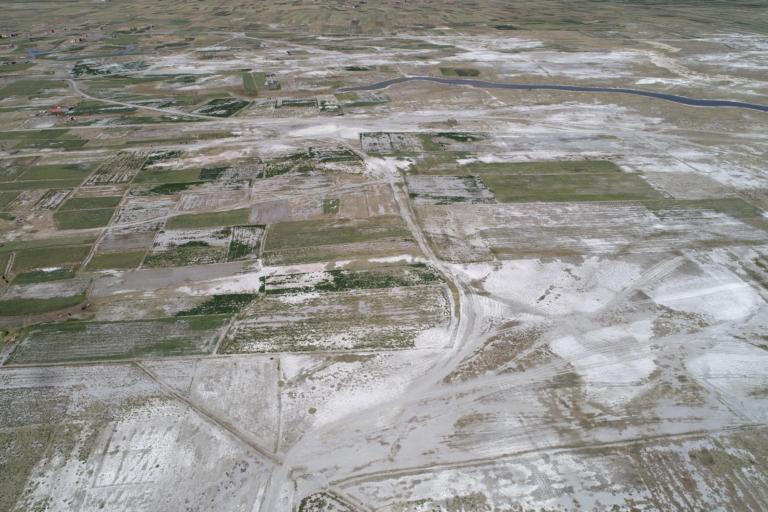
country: BO
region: La Paz
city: Achacachi
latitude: -16.0123
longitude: -68.7262
